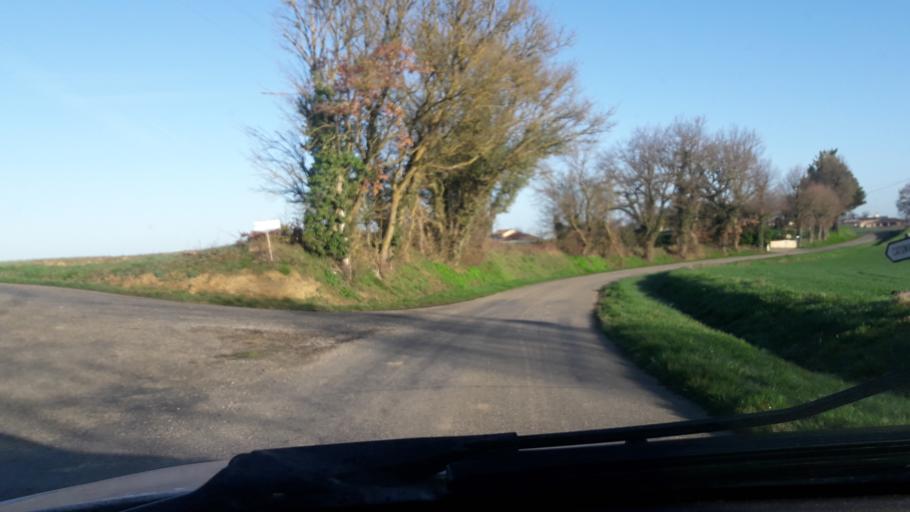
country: FR
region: Midi-Pyrenees
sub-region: Departement du Gers
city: Gimont
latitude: 43.6529
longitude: 0.9653
